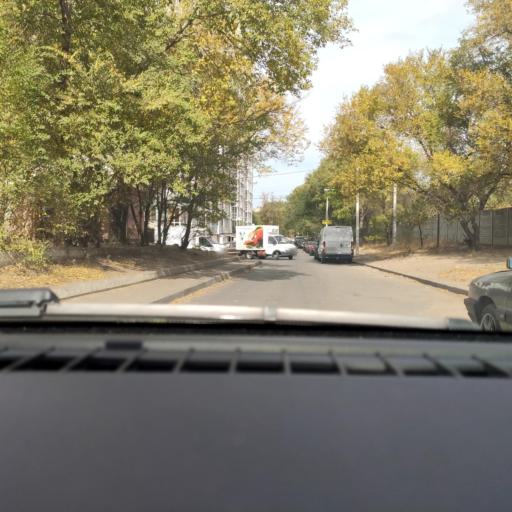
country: RU
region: Voronezj
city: Voronezh
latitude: 51.7121
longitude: 39.2713
